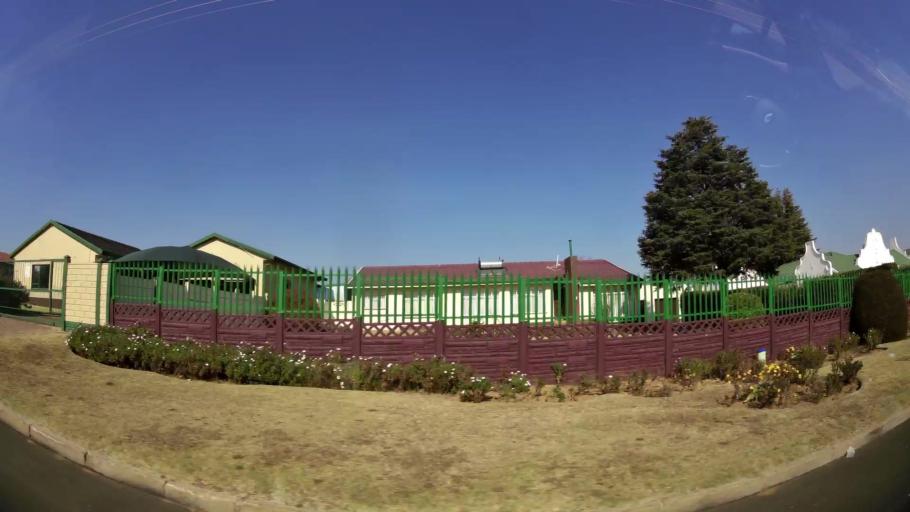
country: ZA
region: Gauteng
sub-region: West Rand District Municipality
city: Randfontein
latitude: -26.1586
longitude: 27.6954
